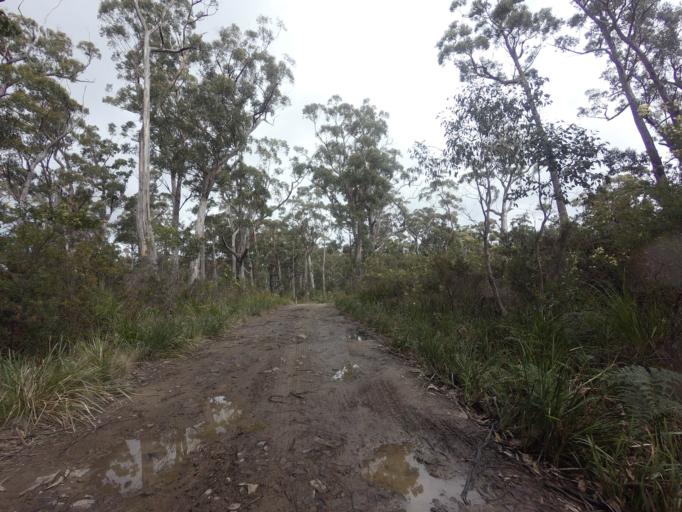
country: AU
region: Tasmania
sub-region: Huon Valley
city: Geeveston
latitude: -43.4645
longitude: 146.9242
